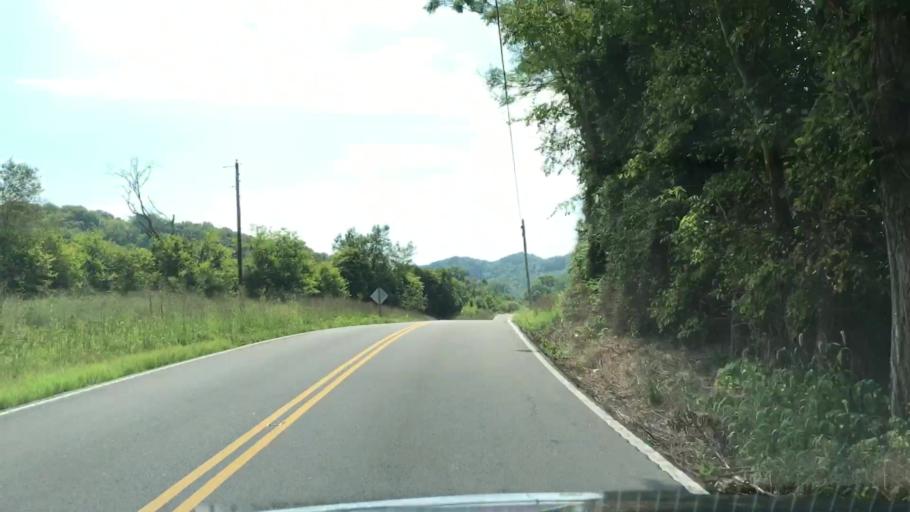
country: US
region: Tennessee
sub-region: Trousdale County
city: Hartsville
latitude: 36.4733
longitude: -86.1804
